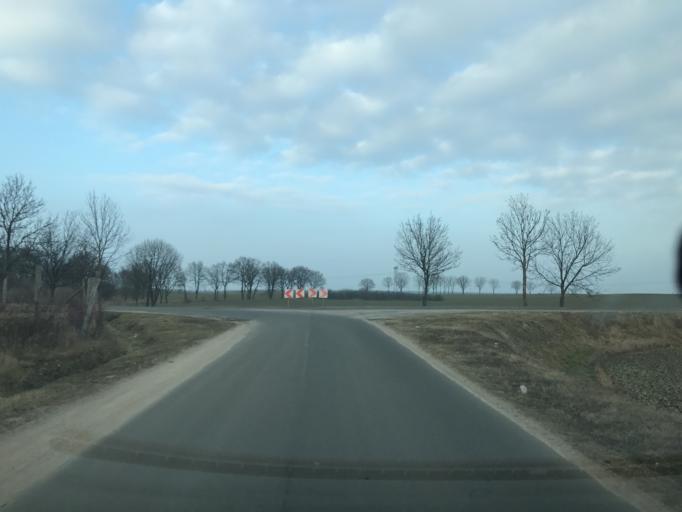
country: PL
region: Kujawsko-Pomorskie
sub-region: Powiat golubsko-dobrzynski
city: Kowalewo Pomorskie
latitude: 53.1883
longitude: 18.9799
